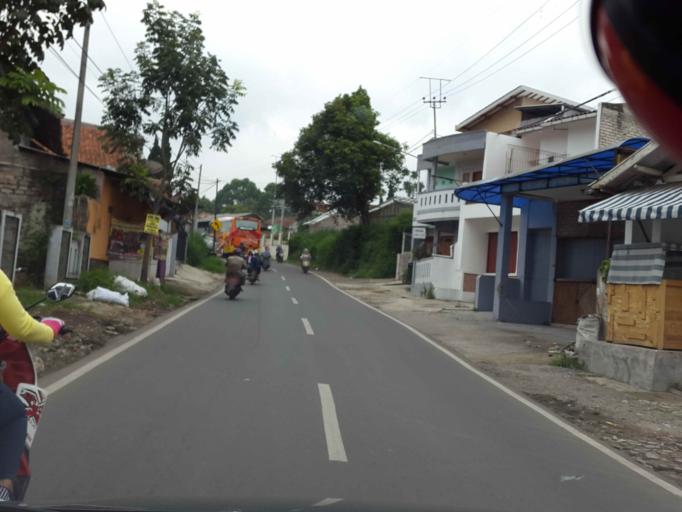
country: ID
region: West Java
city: Lembang
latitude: -6.8076
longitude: 107.5970
